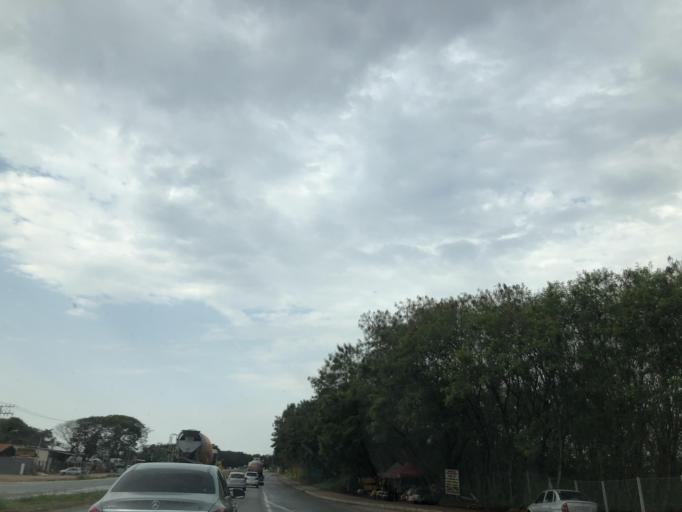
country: BR
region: Sao Paulo
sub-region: Salto De Pirapora
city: Salto de Pirapora
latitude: -23.5824
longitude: -47.5298
